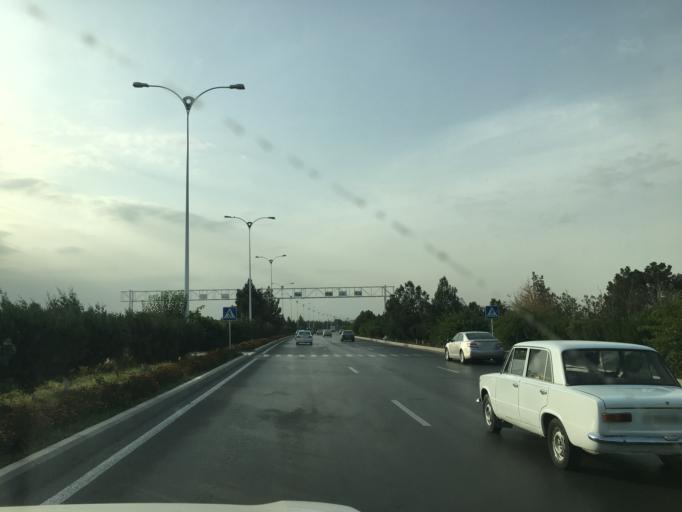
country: TM
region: Ahal
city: Annau
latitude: 37.9191
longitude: 58.4539
